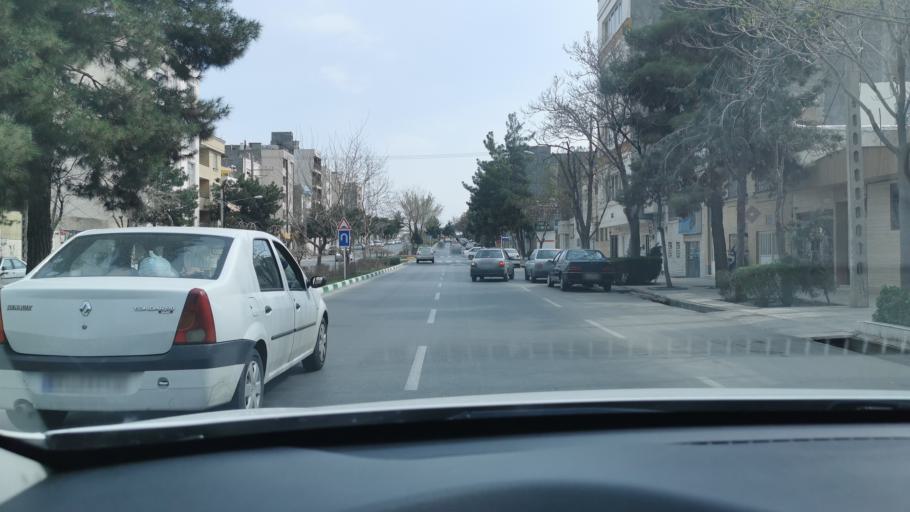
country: IR
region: Razavi Khorasan
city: Mashhad
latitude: 36.2772
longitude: 59.5659
